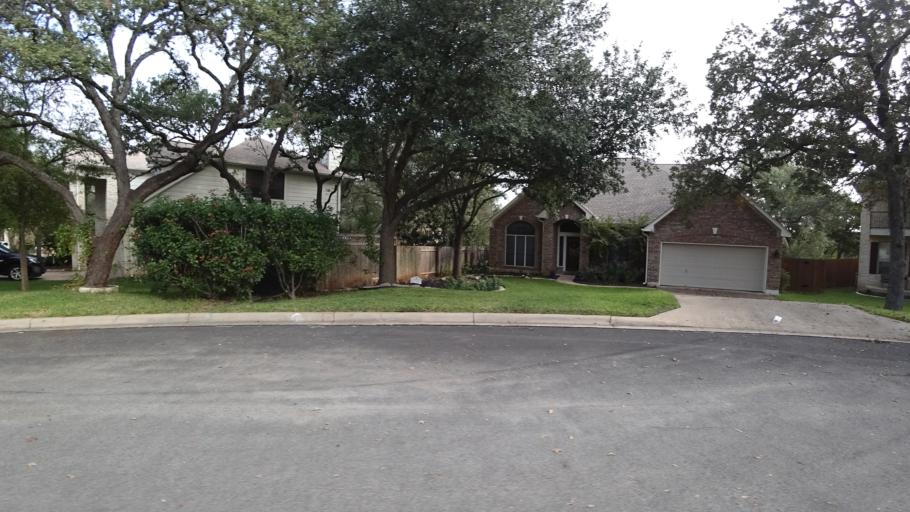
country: US
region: Texas
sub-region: Travis County
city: Shady Hollow
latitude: 30.1883
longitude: -97.8823
